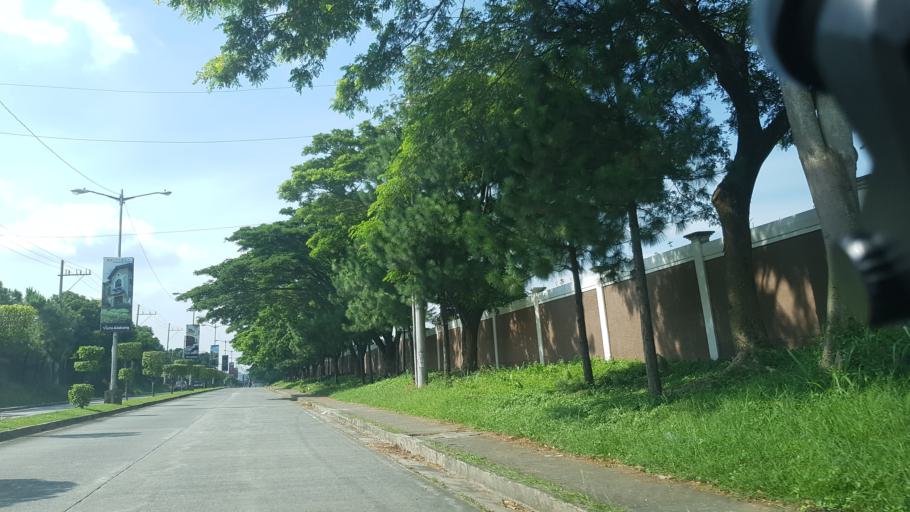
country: PH
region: Calabarzon
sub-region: Province of Laguna
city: Magsaysay
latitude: 14.3628
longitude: 121.0096
